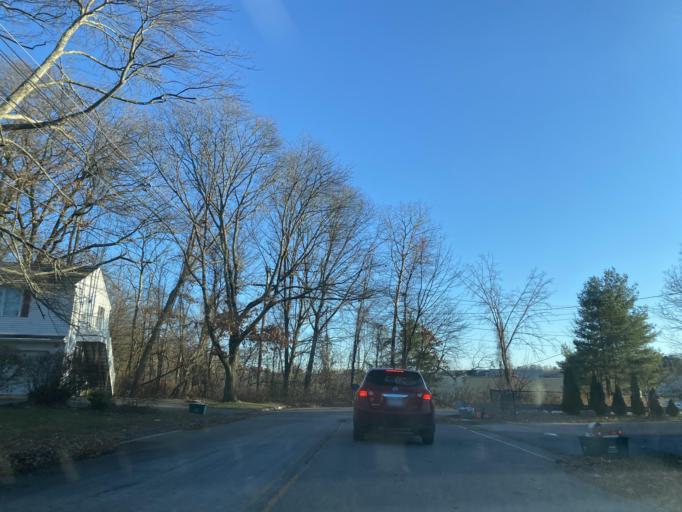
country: US
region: Massachusetts
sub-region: Worcester County
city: Hamilton
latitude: 42.2500
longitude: -71.7608
